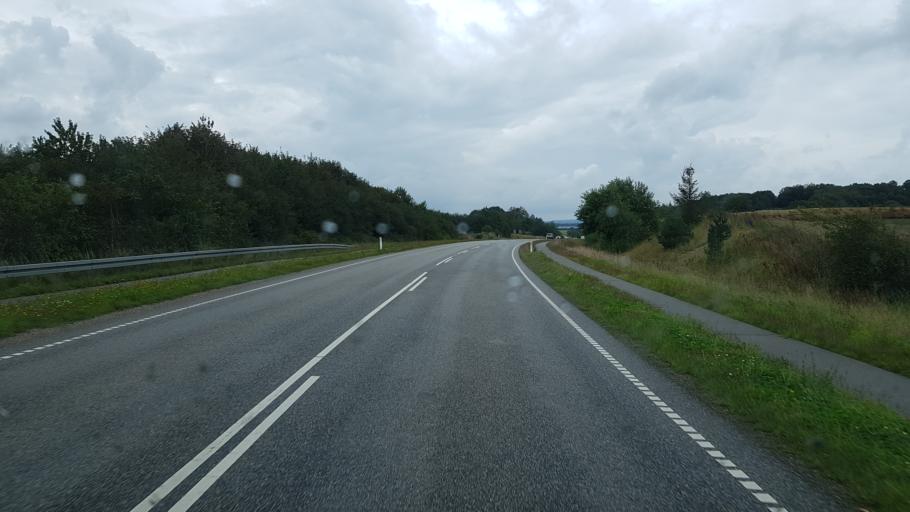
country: DK
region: Central Jutland
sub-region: Horsens Kommune
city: Horsens
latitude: 55.9029
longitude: 9.7445
